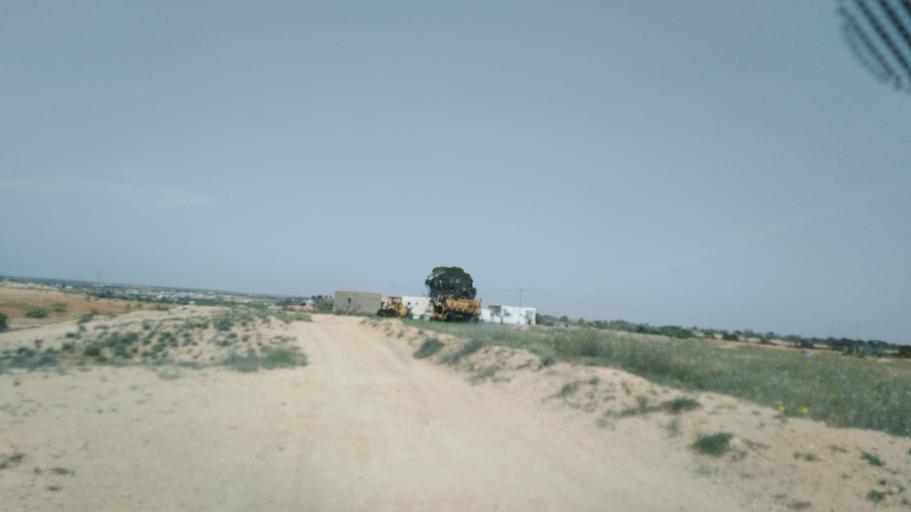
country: TN
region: Safaqis
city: Sfax
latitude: 34.7204
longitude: 10.5663
